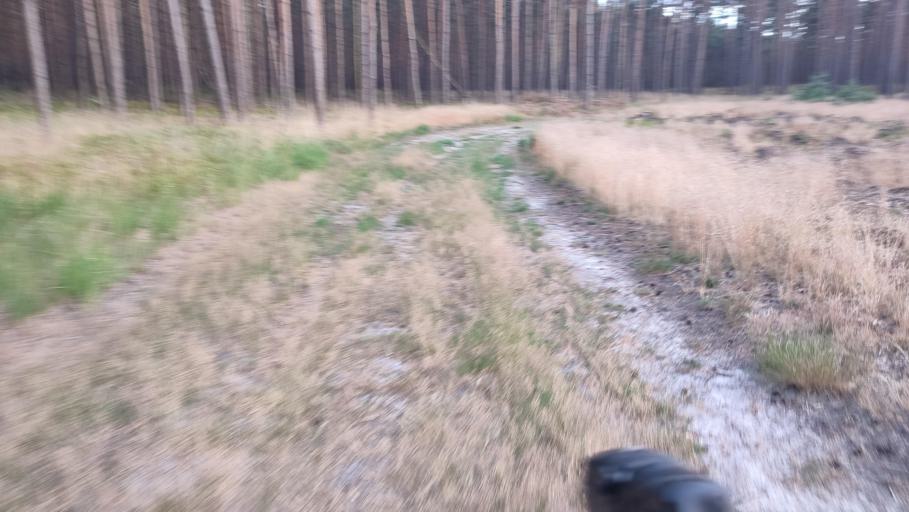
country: DE
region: Lower Saxony
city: Hitzacker
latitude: 53.2165
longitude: 11.0402
